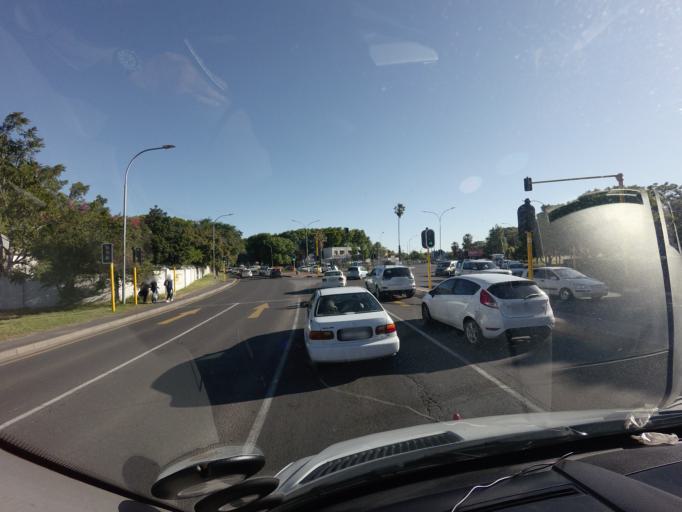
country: ZA
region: Western Cape
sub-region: Cape Winelands District Municipality
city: Stellenbosch
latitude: -33.9366
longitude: 18.8517
